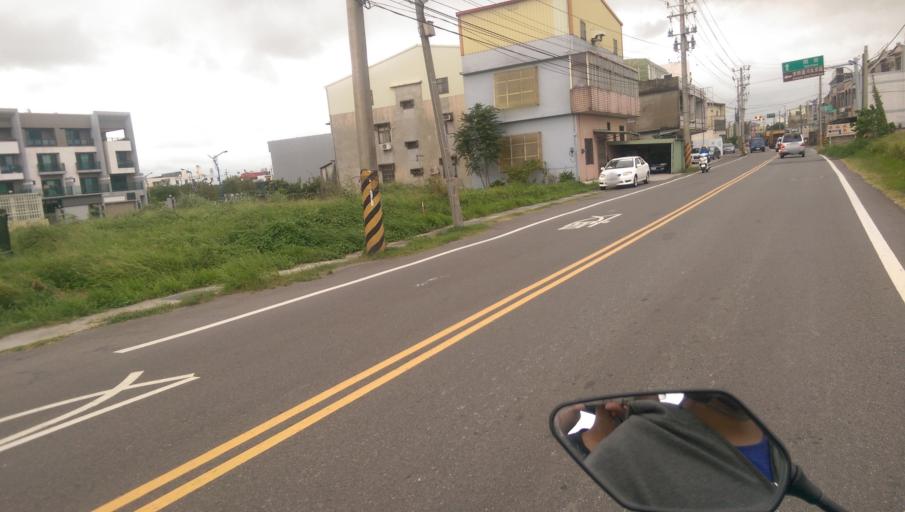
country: TW
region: Taiwan
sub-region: Hsinchu
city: Hsinchu
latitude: 24.8167
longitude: 120.9290
